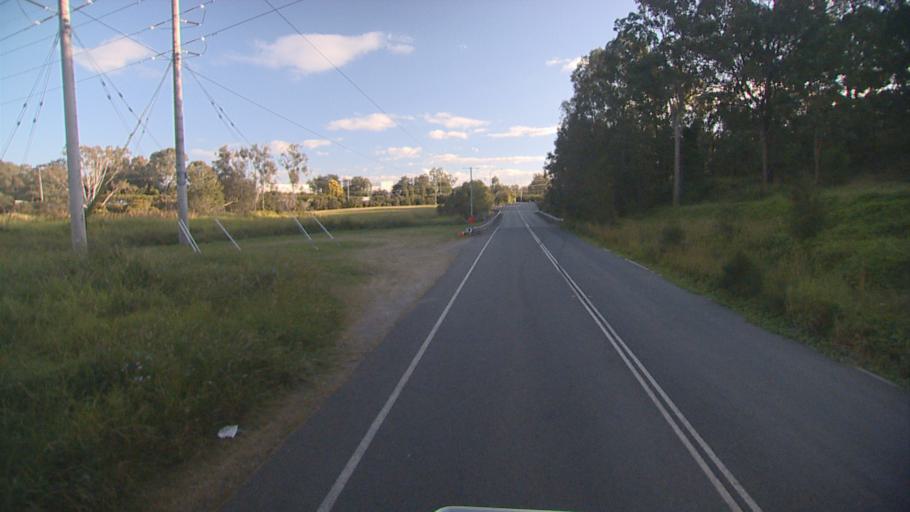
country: AU
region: Queensland
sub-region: Logan
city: Beenleigh
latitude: -27.7110
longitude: 153.1809
